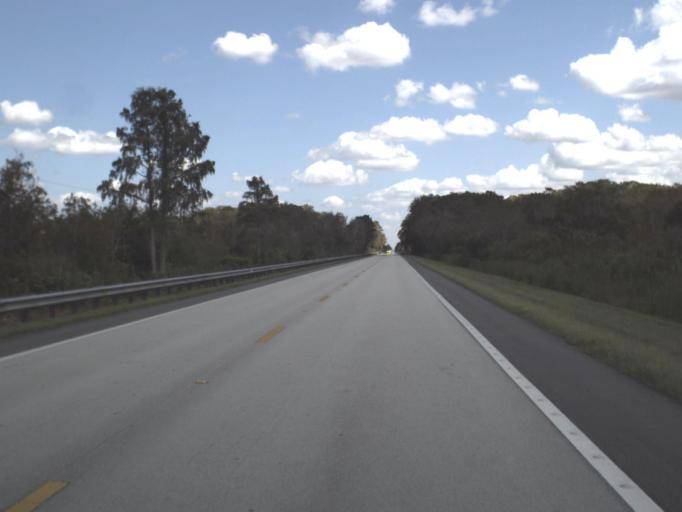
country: US
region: Florida
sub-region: Miami-Dade County
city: Kendall West
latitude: 25.8600
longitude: -81.0641
